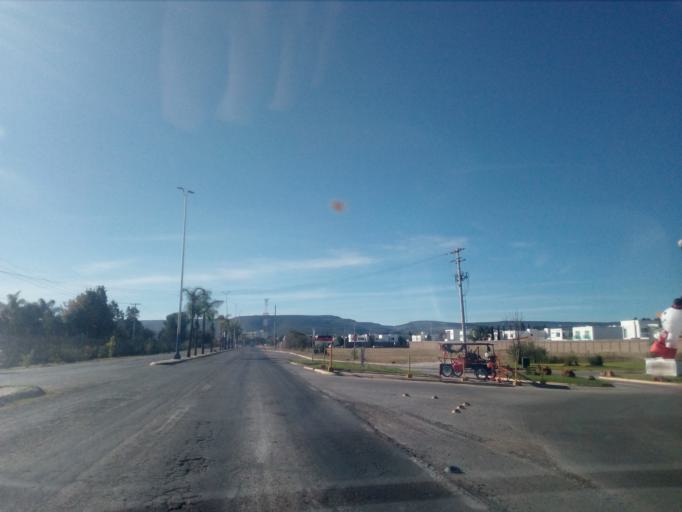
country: MX
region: Durango
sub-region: Durango
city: Sebastian Lerdo de Tejada
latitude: 23.9752
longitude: -104.6648
